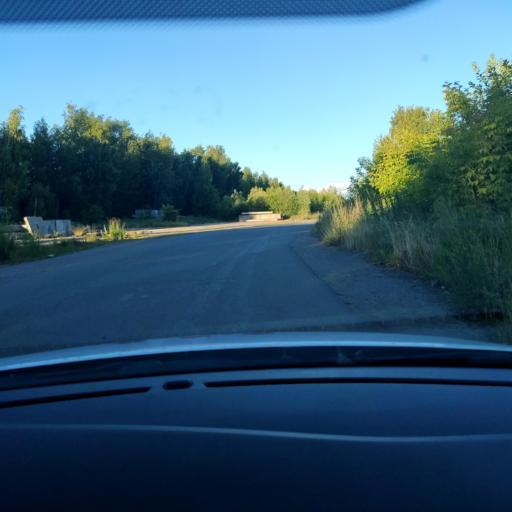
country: RU
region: Tatarstan
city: Staroye Arakchino
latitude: 55.8622
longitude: 48.9464
